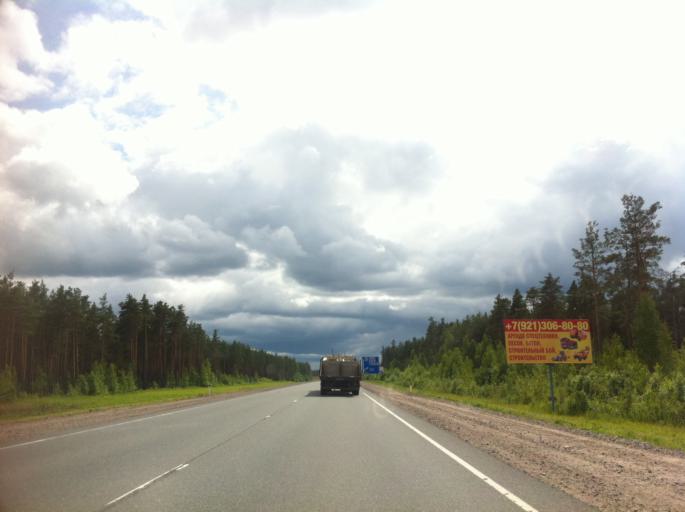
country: RU
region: Leningrad
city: Luga
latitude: 58.7407
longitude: 29.8908
